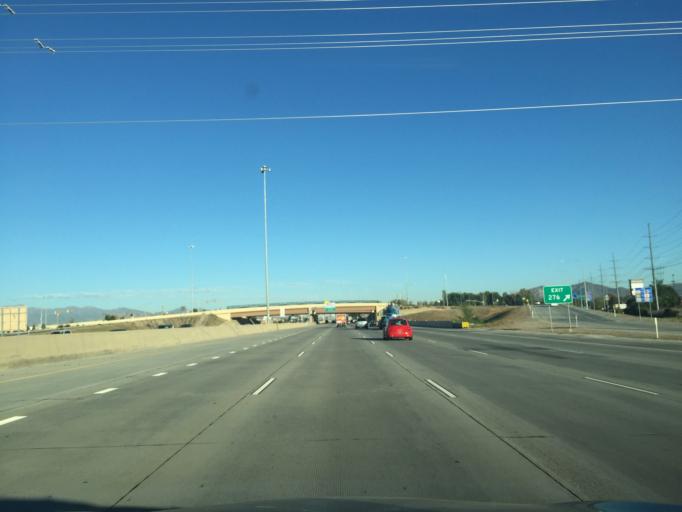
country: US
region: Utah
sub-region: Utah County
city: American Fork
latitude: 40.3589
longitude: -111.7826
